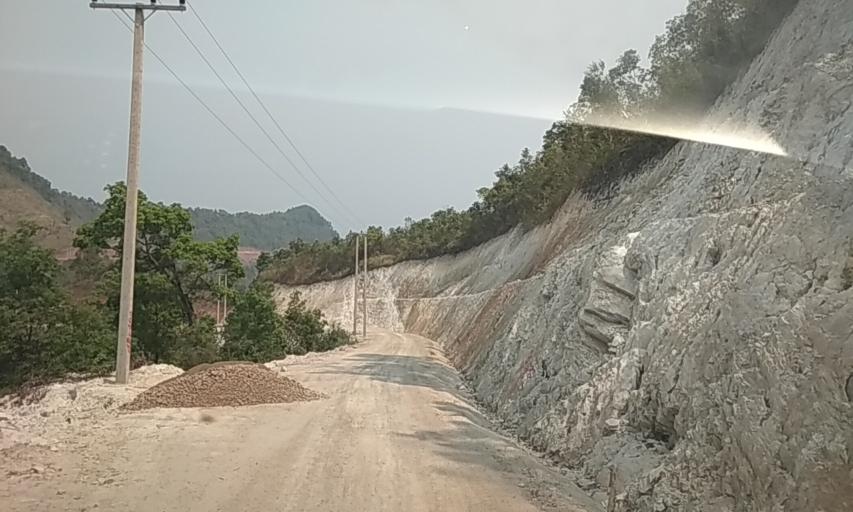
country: VN
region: Huyen Dien Bien
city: Dien Bien Phu
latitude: 21.4887
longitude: 102.7856
